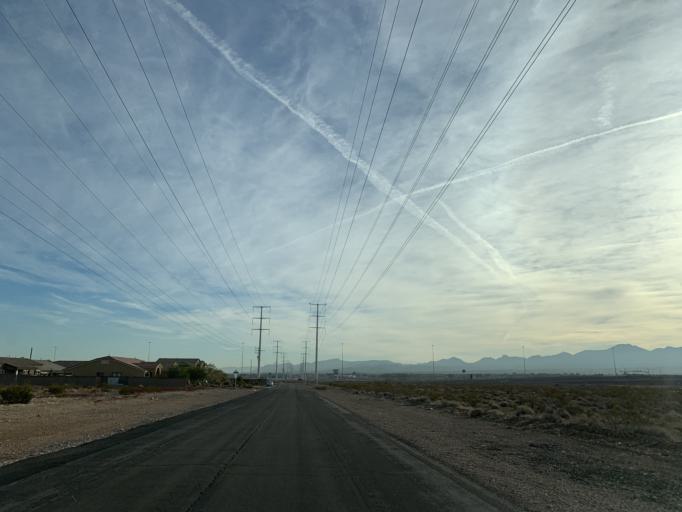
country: US
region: Nevada
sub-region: Clark County
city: Enterprise
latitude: 36.0025
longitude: -115.1868
